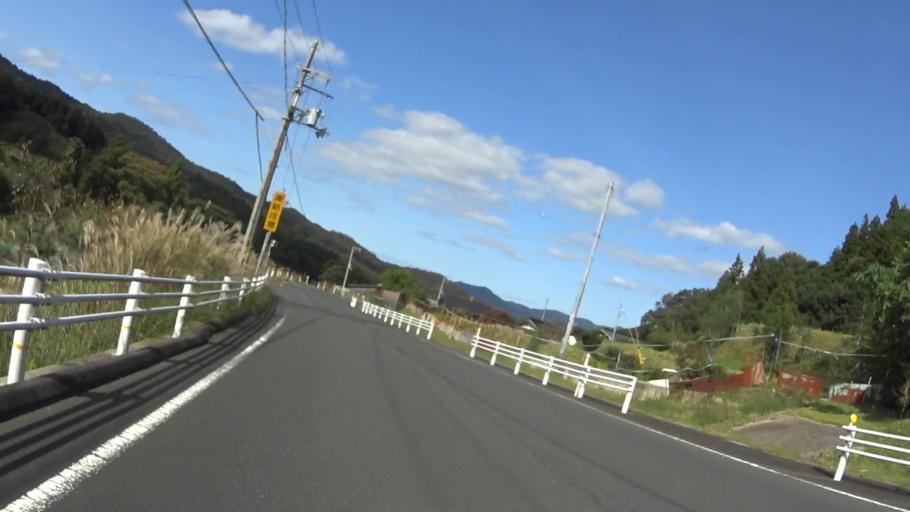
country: JP
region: Hyogo
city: Toyooka
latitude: 35.5427
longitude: 134.9781
